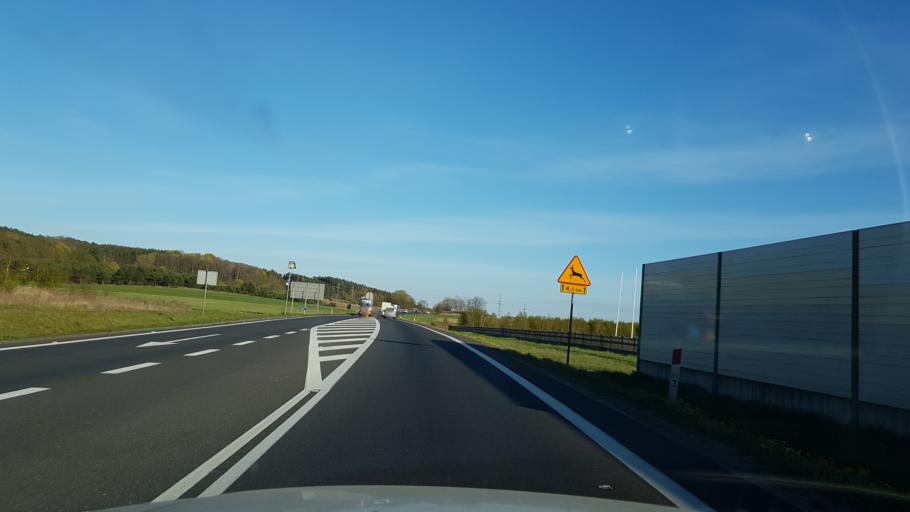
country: PL
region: West Pomeranian Voivodeship
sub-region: Powiat kamienski
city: Wolin
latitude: 53.8681
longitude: 14.5447
